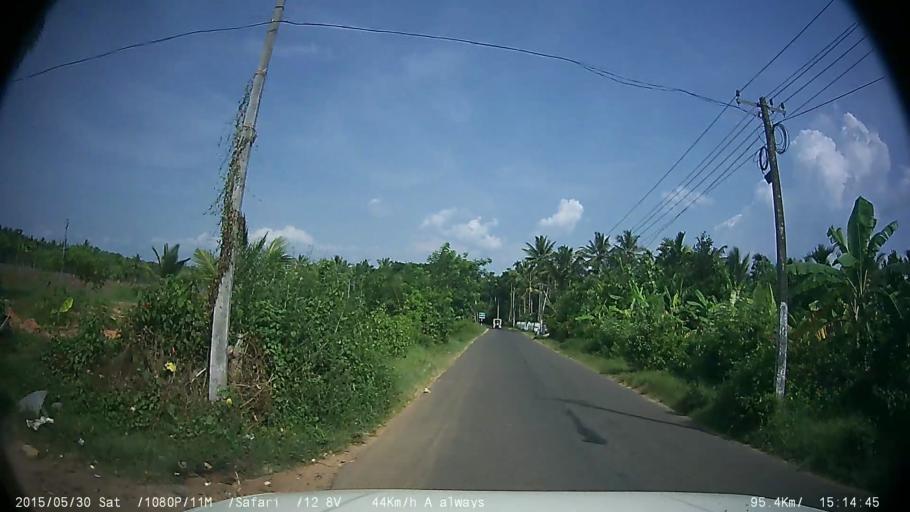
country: IN
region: Kerala
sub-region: Wayanad
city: Panamaram
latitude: 11.7835
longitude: 76.0457
